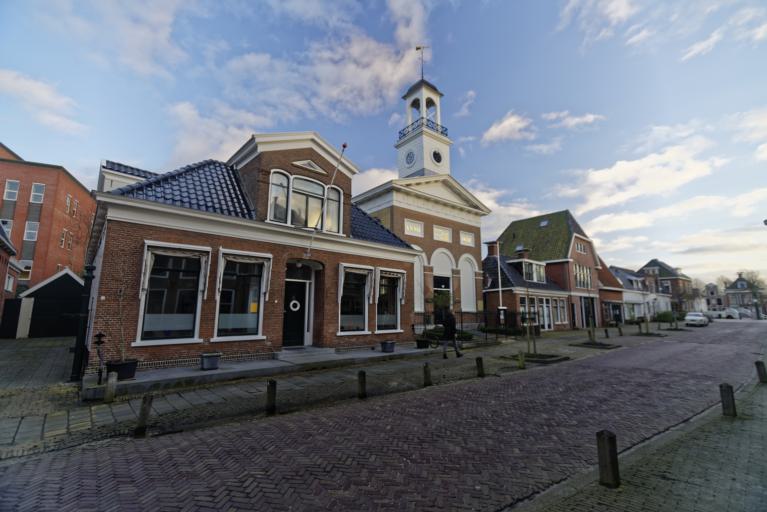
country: NL
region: Friesland
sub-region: Gemeente Dongeradeel
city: Dokkum
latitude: 53.3258
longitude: 5.9960
